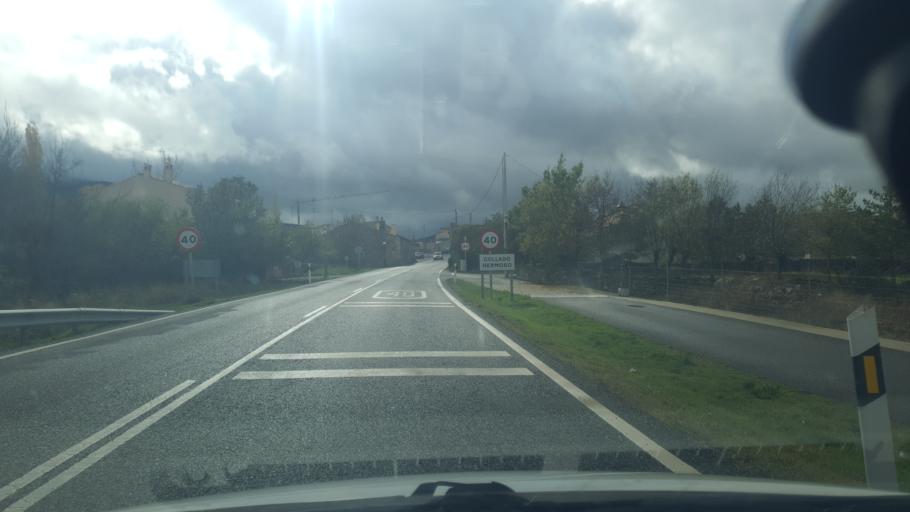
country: ES
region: Castille and Leon
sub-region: Provincia de Segovia
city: Collado Hermoso
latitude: 41.0409
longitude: -3.9165
